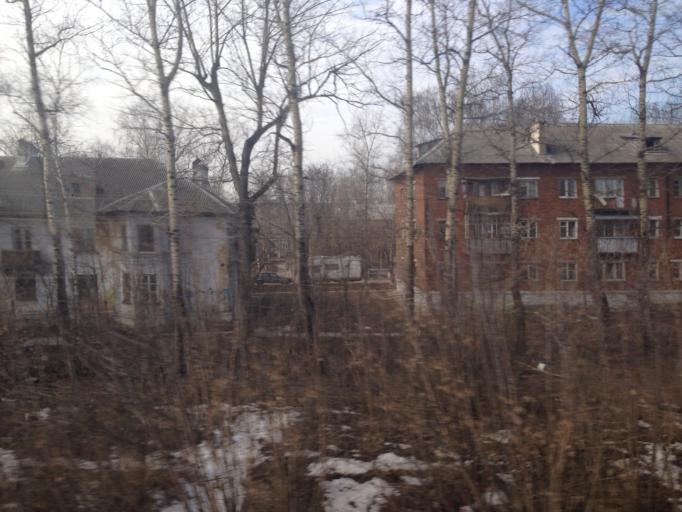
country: RU
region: Moskovskaya
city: Sheremet'yevskiy
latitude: 55.9740
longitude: 37.5034
